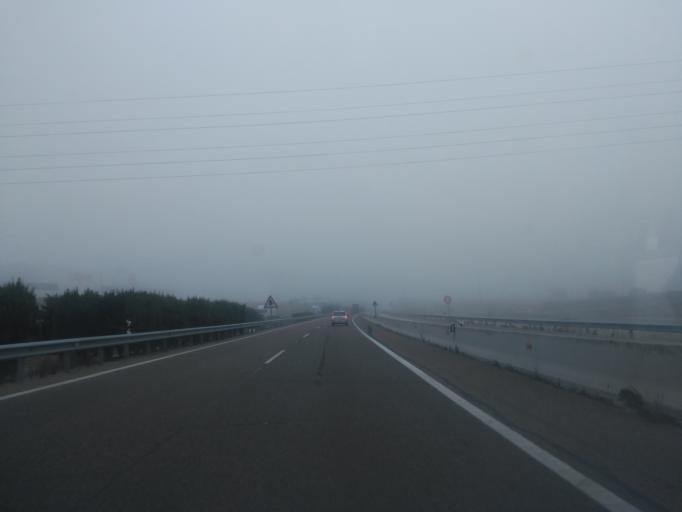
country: ES
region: Castille and Leon
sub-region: Provincia de Valladolid
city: Arroyo
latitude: 41.6245
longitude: -4.7873
